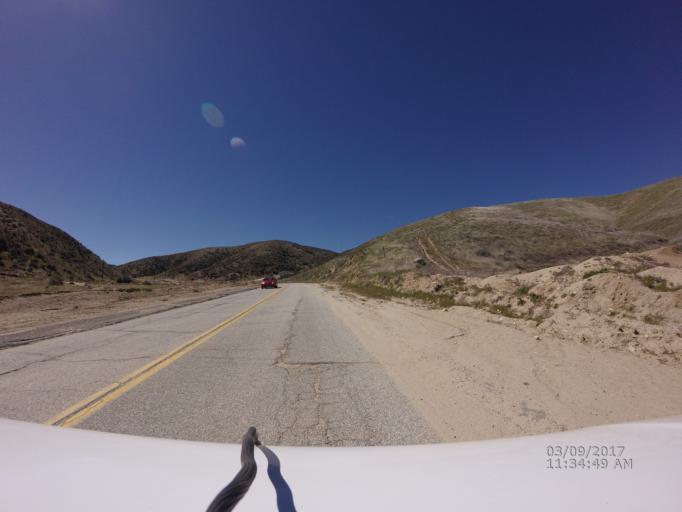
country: US
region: California
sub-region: Los Angeles County
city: Green Valley
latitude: 34.6825
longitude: -118.3906
